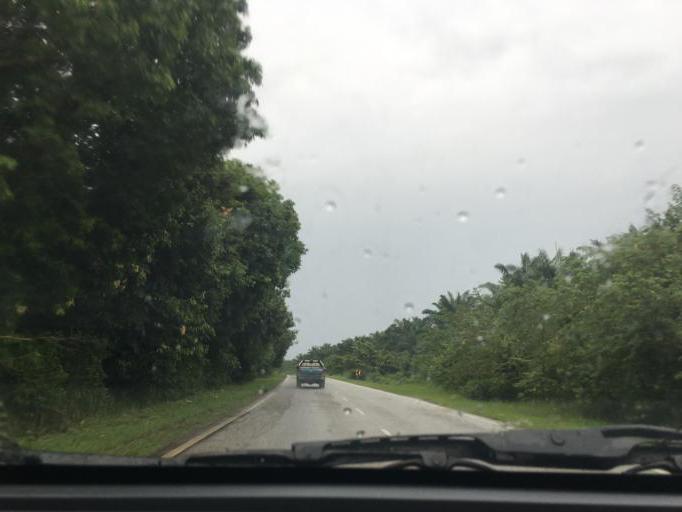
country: MY
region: Kedah
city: Sungai Petani
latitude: 5.6315
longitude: 100.6316
